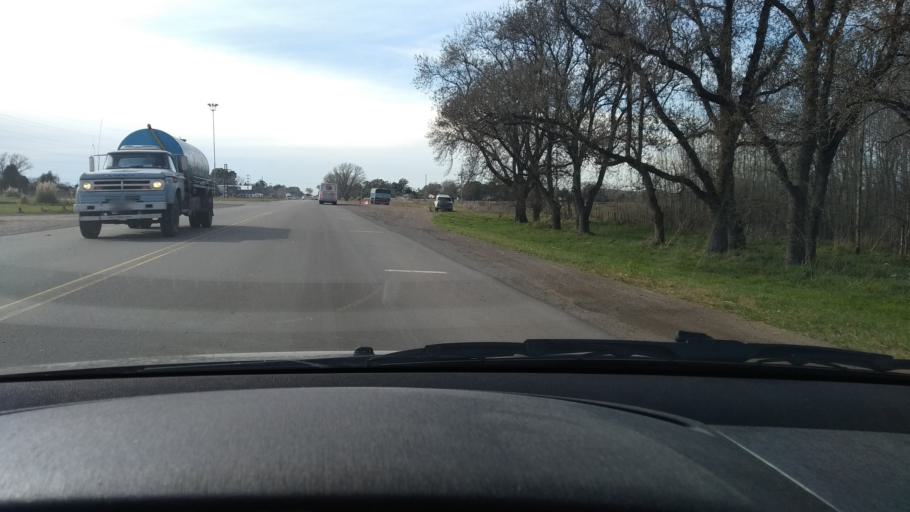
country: AR
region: Buenos Aires
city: Olavarria
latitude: -36.9569
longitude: -60.2556
